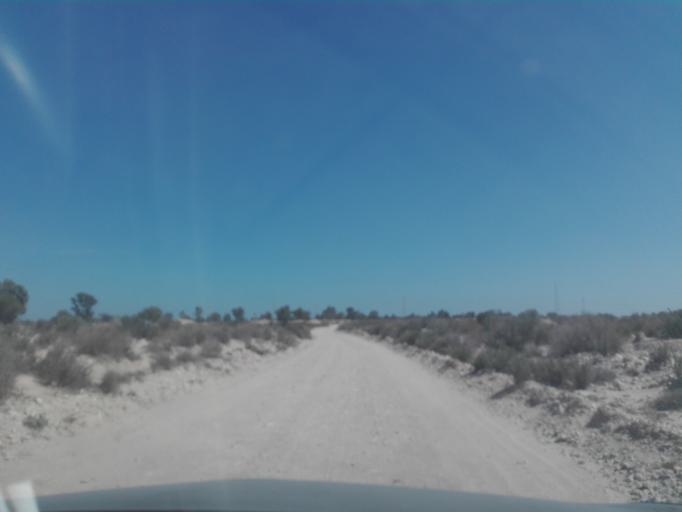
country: TN
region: Qabis
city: Gabes
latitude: 33.8748
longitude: 10.0233
